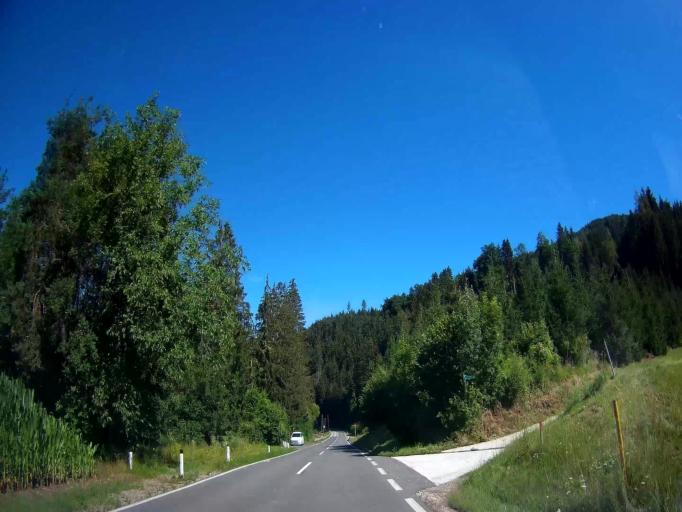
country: AT
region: Carinthia
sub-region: Politischer Bezirk Sankt Veit an der Glan
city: Bruckl
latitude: 46.7589
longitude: 14.4959
